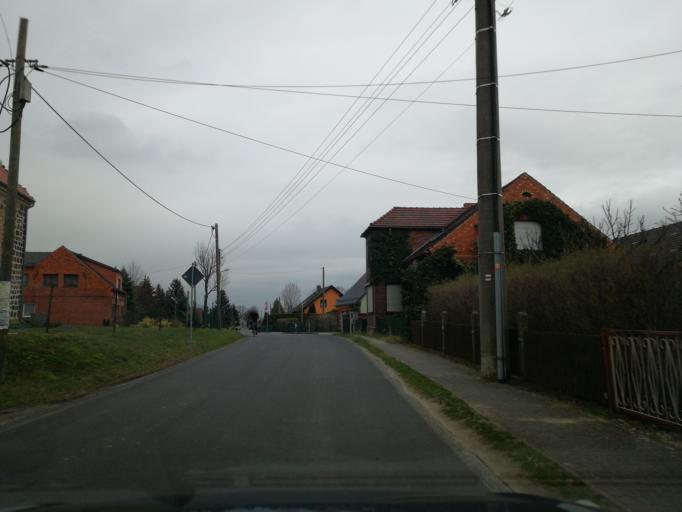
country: DE
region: Brandenburg
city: Calau
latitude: 51.7300
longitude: 14.0178
